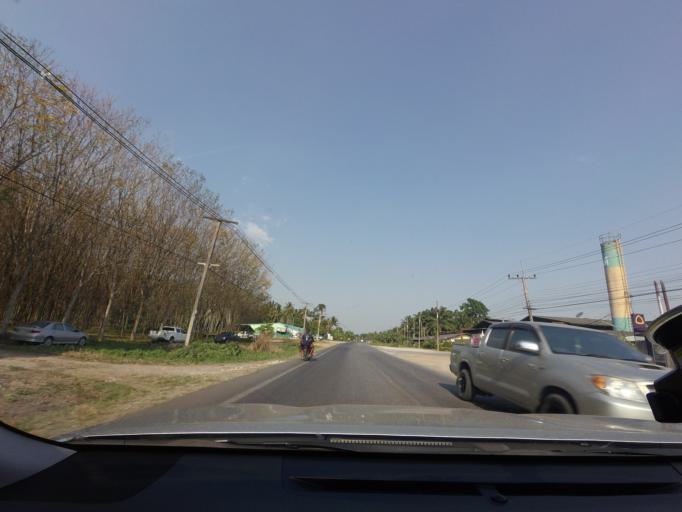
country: TH
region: Surat Thani
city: Phrasaeng
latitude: 8.5660
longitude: 99.1869
